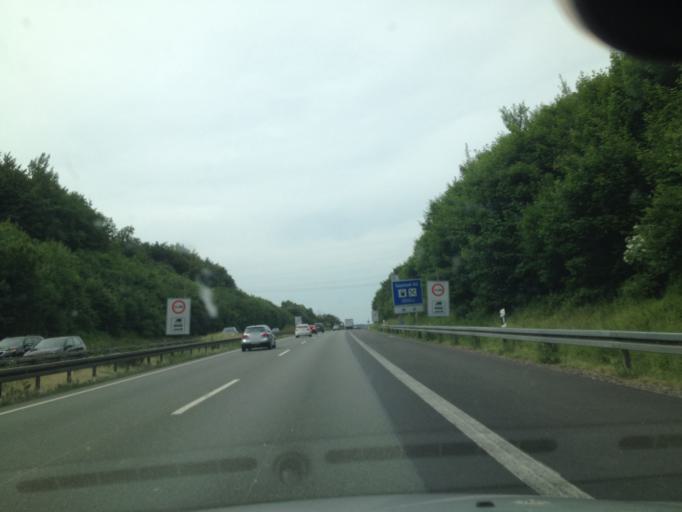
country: DE
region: North Rhine-Westphalia
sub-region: Regierungsbezirk Arnsberg
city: Luedenscheid
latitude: 51.2098
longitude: 7.6718
